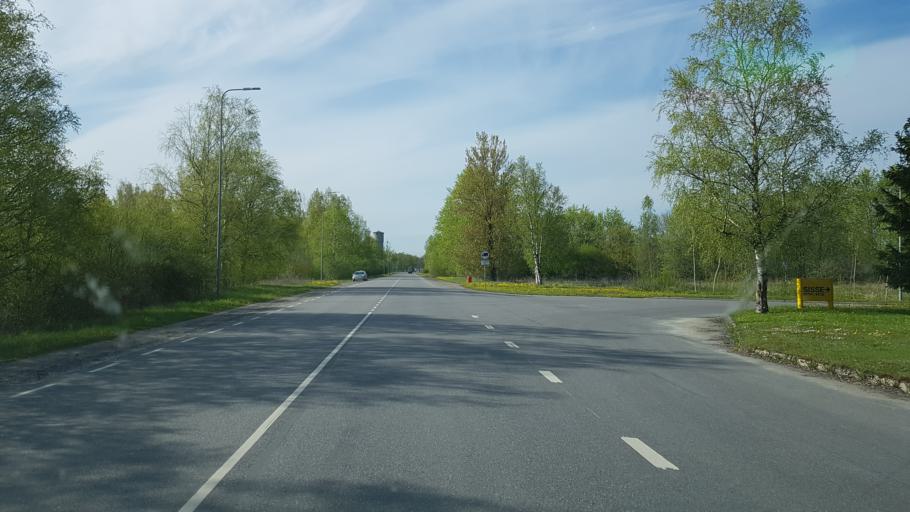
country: EE
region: Ida-Virumaa
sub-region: Kivioli linn
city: Kivioli
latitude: 59.3644
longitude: 26.9690
